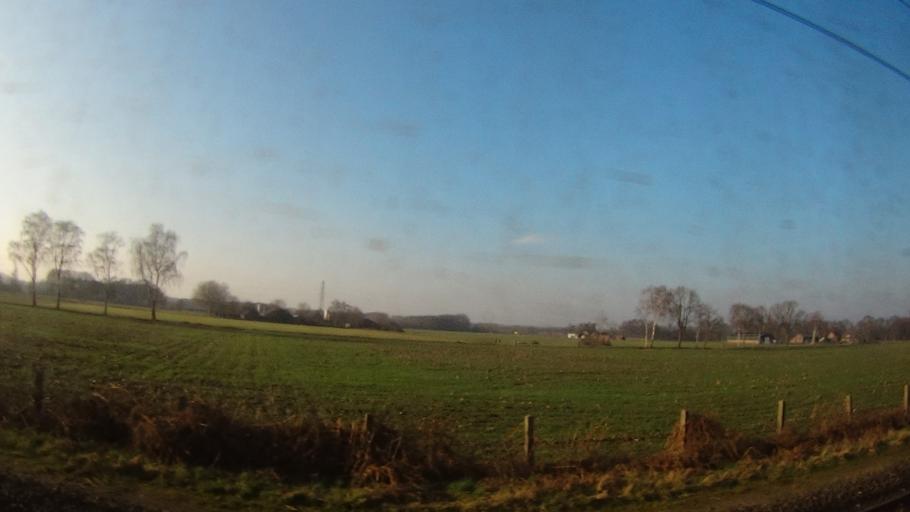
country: NL
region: Gelderland
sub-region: Gemeente Putten
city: Putten
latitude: 52.2680
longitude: 5.5792
